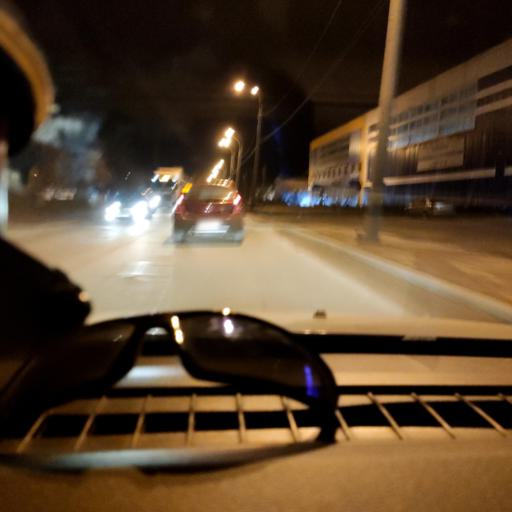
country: RU
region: Samara
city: Samara
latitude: 53.1343
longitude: 50.1173
